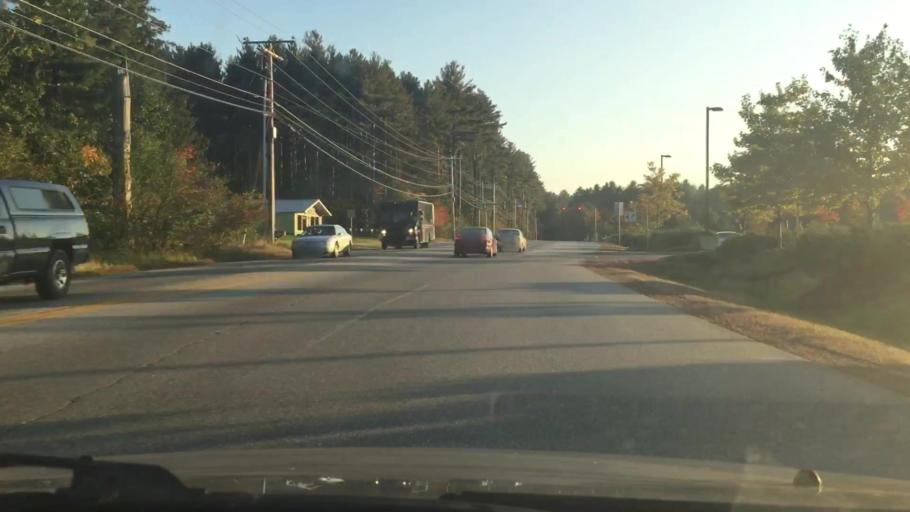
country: US
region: New Hampshire
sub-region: Cheshire County
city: Keene
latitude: 42.9105
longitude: -72.2950
